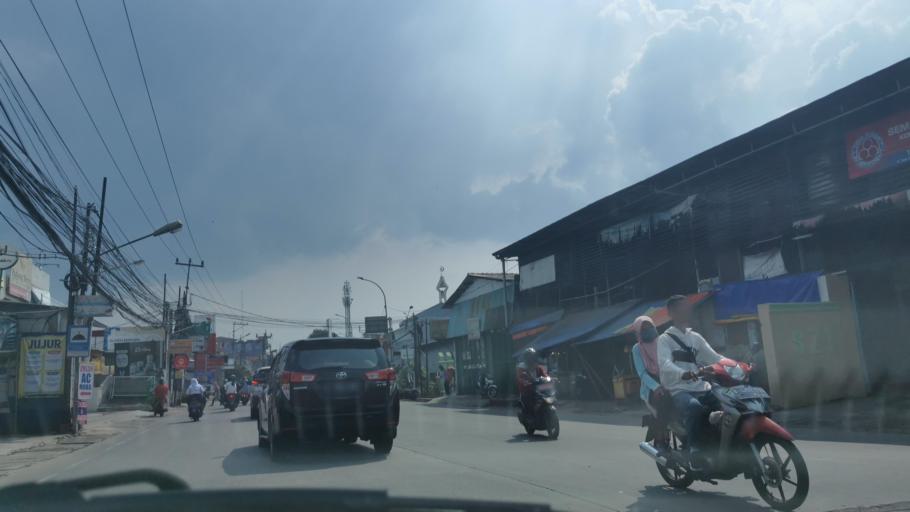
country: ID
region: West Java
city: Depok
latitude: -6.4034
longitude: 106.8391
